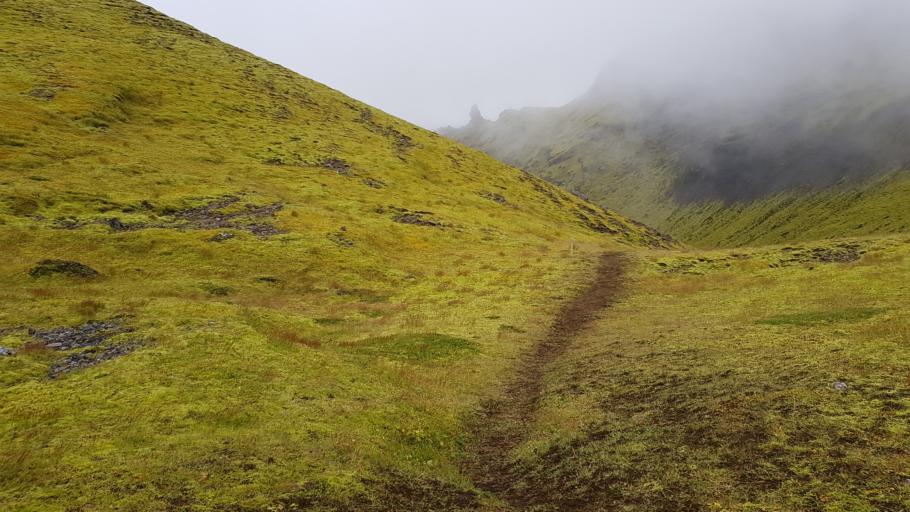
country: IS
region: South
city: Vestmannaeyjar
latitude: 63.5372
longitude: -18.8543
